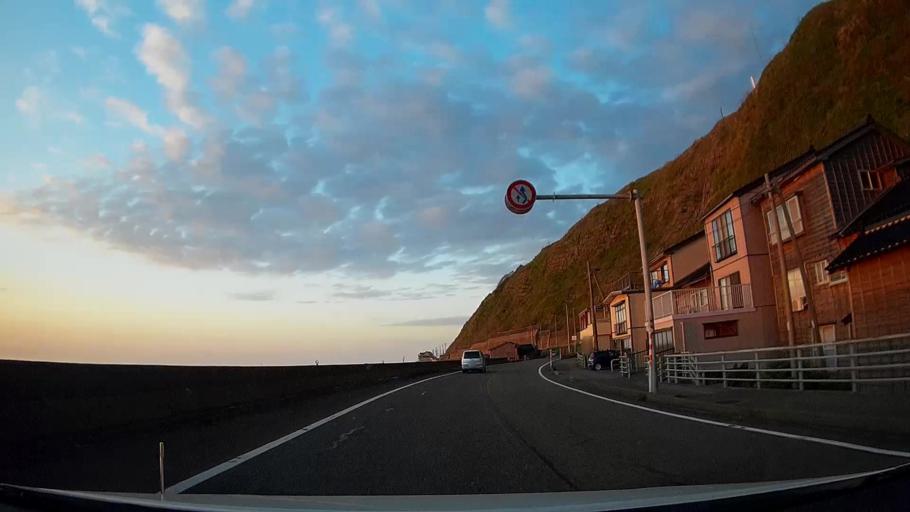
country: JP
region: Niigata
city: Joetsu
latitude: 37.1377
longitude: 138.0579
